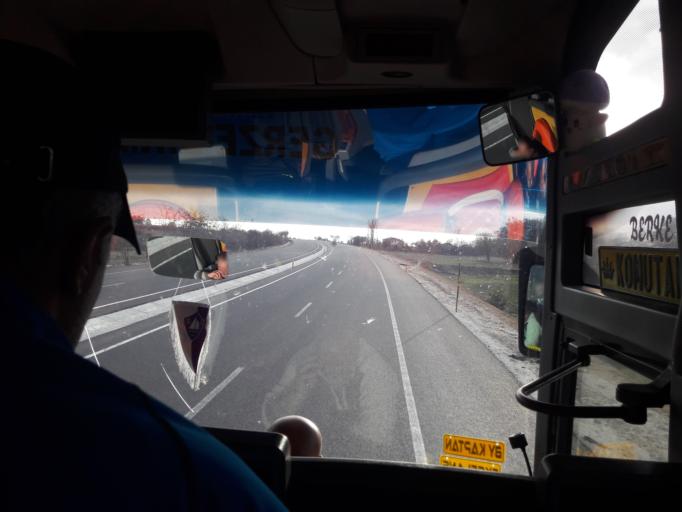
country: TR
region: Cankiri
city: Ilgaz
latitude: 40.8578
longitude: 33.6150
